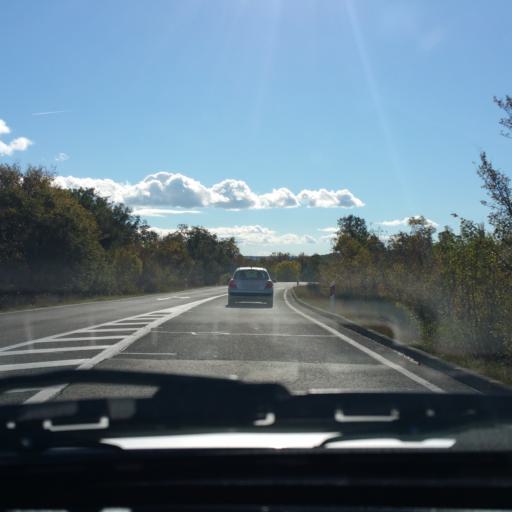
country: HR
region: Primorsko-Goranska
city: Omisalj
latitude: 45.1980
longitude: 14.5630
